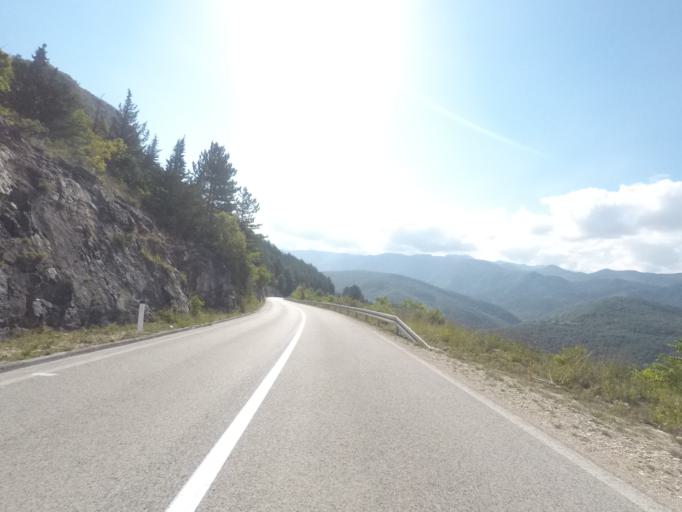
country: BA
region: Republika Srpska
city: Trebinje
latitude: 42.7163
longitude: 18.5033
